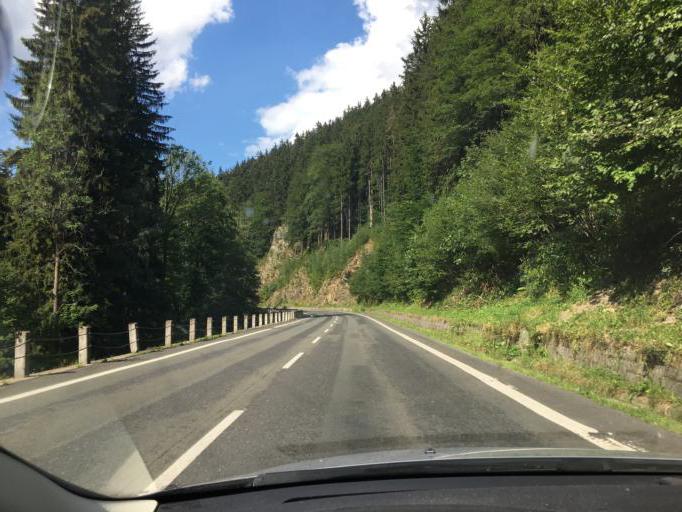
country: CZ
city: Benecko
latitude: 50.6705
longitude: 15.5928
